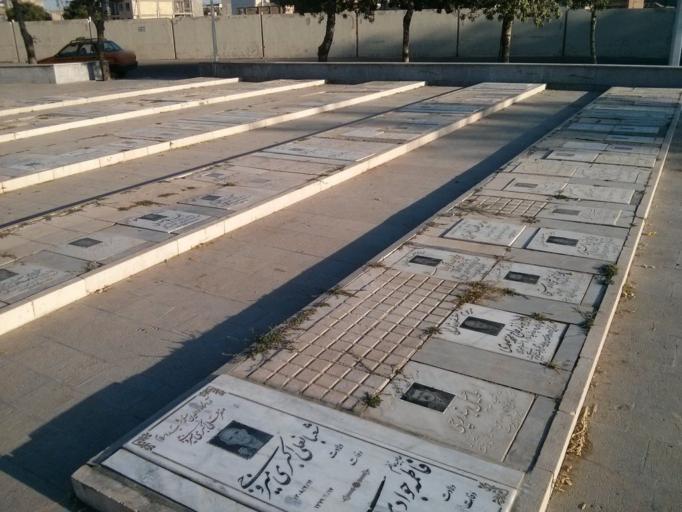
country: IR
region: Qazvin
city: Qazvin
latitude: 36.2570
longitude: 49.9981
